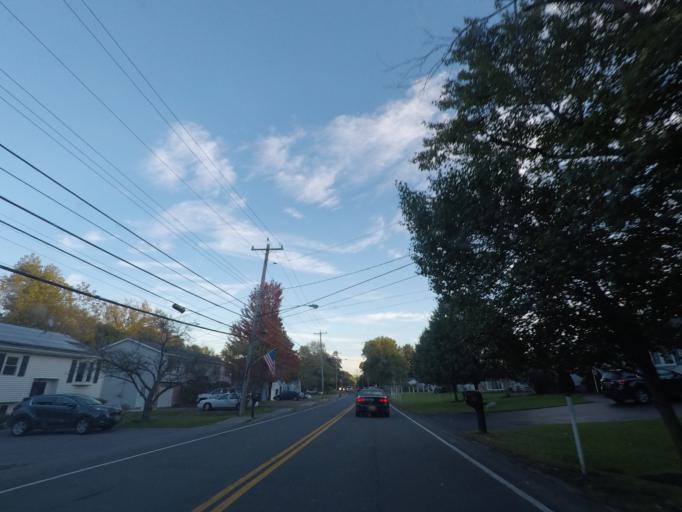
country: US
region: New York
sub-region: Albany County
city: Colonie
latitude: 42.7284
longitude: -73.8258
